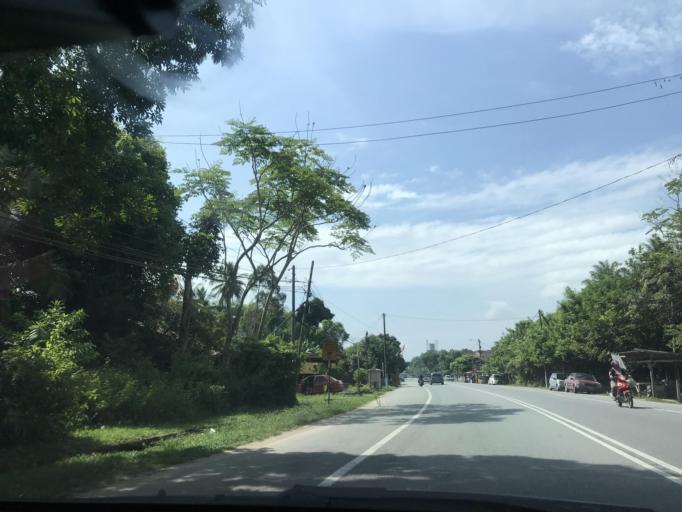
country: MY
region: Kelantan
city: Tumpat
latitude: 6.1392
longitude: 102.1696
